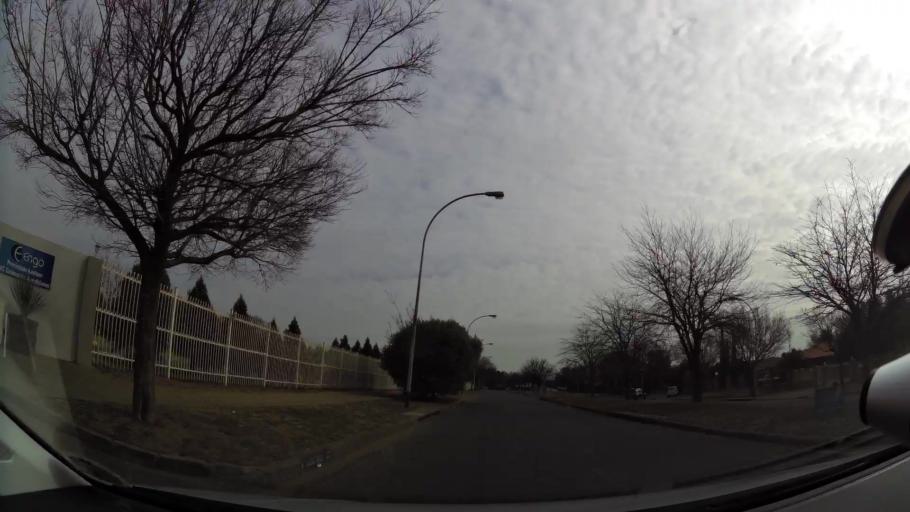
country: ZA
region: Orange Free State
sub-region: Mangaung Metropolitan Municipality
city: Bloemfontein
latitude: -29.1254
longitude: 26.1994
